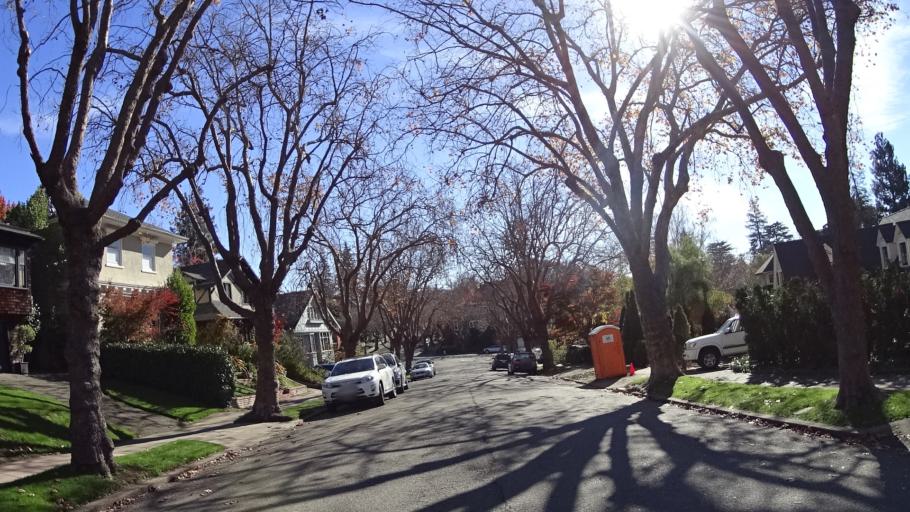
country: US
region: California
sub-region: Alameda County
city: Piedmont
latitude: 37.8278
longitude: -122.2357
